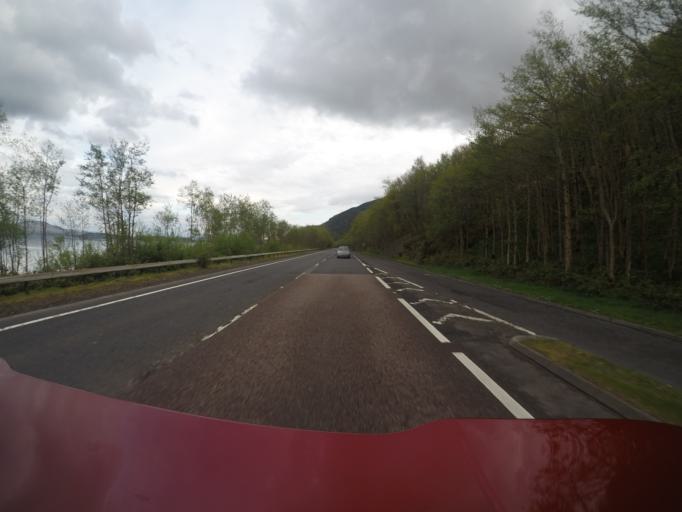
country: GB
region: Scotland
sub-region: Argyll and Bute
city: Helensburgh
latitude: 56.1267
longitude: -4.6538
